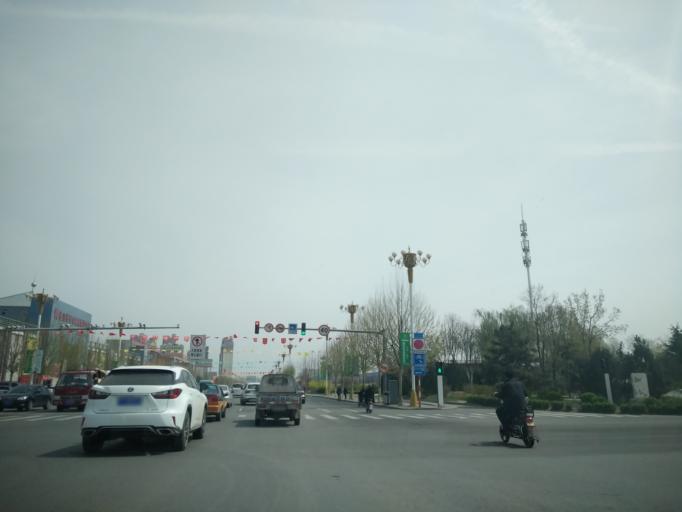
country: CN
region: Beijing
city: Xiji
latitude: 39.7461
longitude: 116.9869
